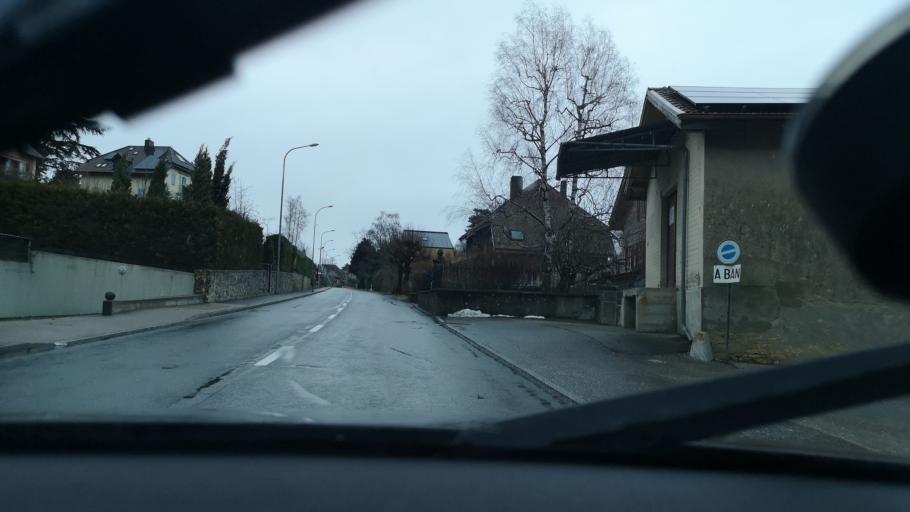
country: CH
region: Neuchatel
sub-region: Boudry District
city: Bevaix
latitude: 46.9270
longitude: 6.8118
